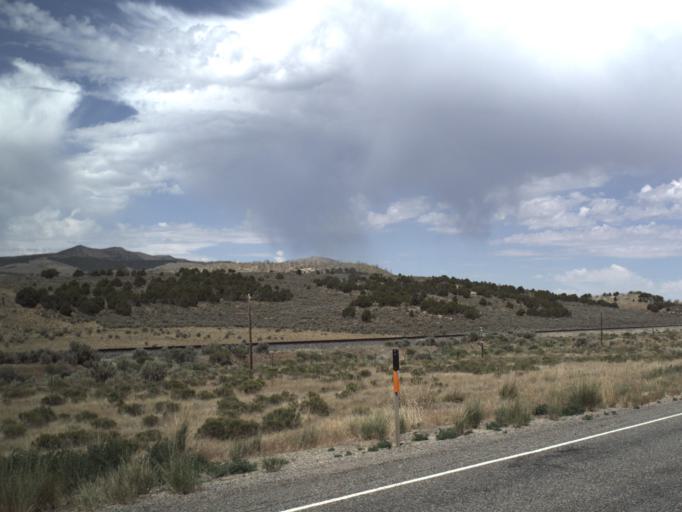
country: US
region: Utah
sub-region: Utah County
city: Genola
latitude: 39.9484
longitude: -112.2341
